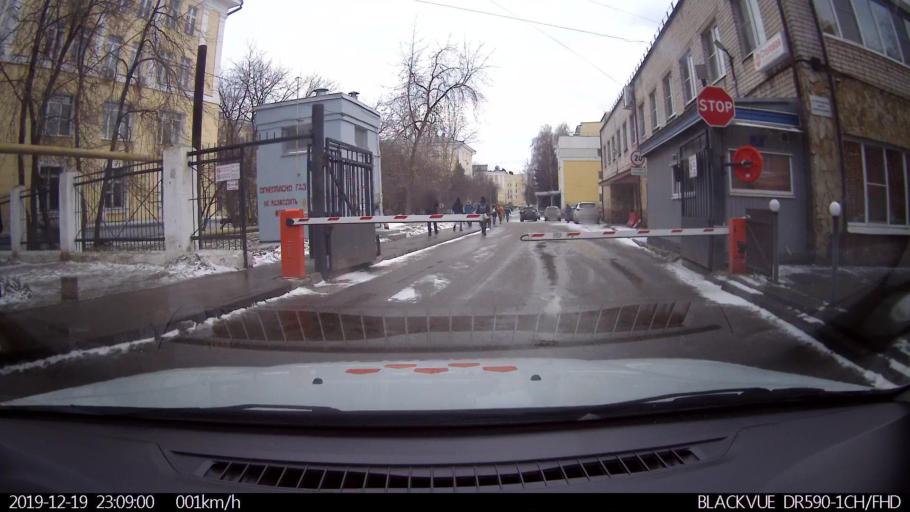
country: RU
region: Nizjnij Novgorod
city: Nizhniy Novgorod
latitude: 56.3003
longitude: 43.9817
